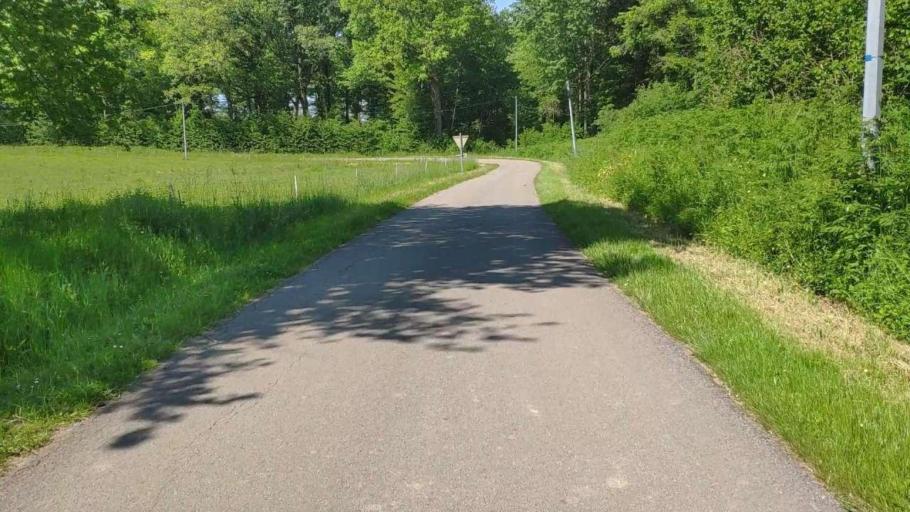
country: FR
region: Franche-Comte
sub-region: Departement du Jura
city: Bletterans
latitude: 46.8109
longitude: 5.4113
